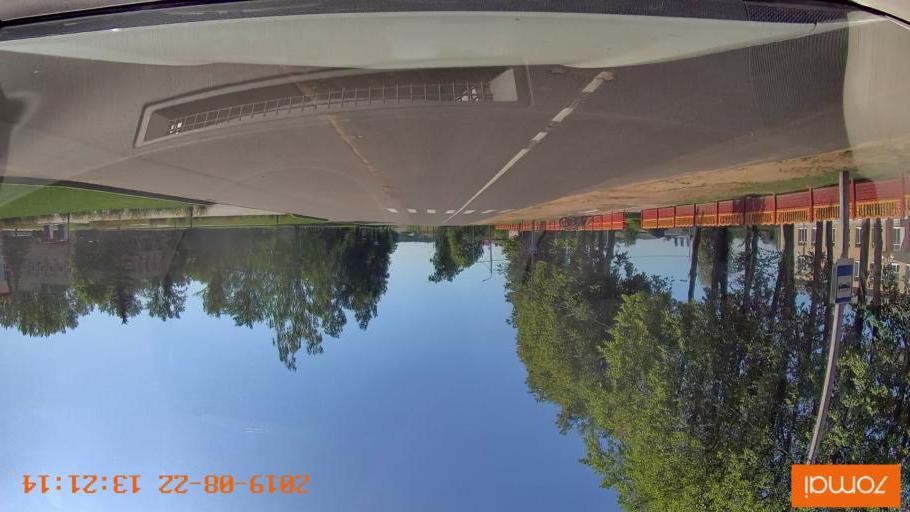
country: BY
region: Minsk
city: Urechcha
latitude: 53.2256
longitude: 27.9783
